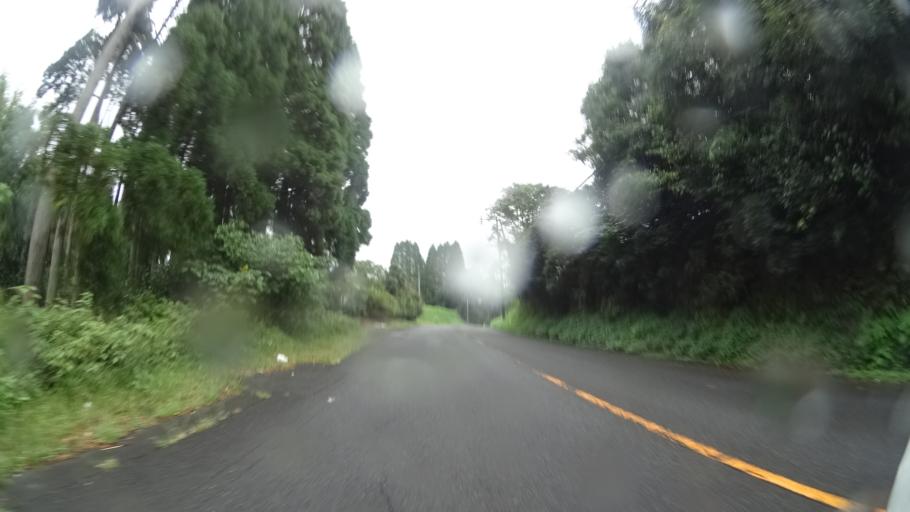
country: JP
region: Kagoshima
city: Kajiki
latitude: 31.7843
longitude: 130.6743
